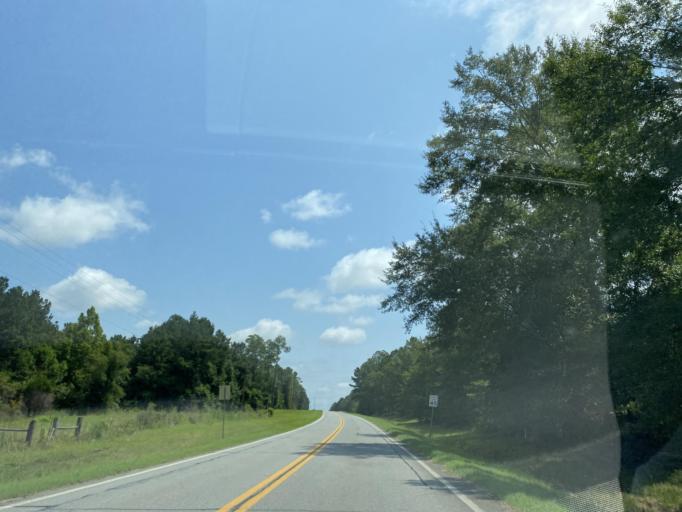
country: US
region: Georgia
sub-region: Wilcox County
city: Abbeville
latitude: 31.9918
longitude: -83.1932
